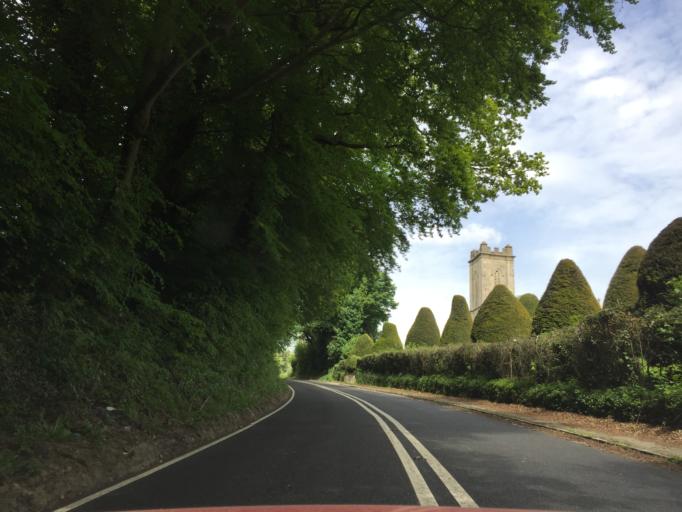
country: GB
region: England
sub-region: Gloucestershire
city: Painswick
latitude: 51.7720
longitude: -2.2171
